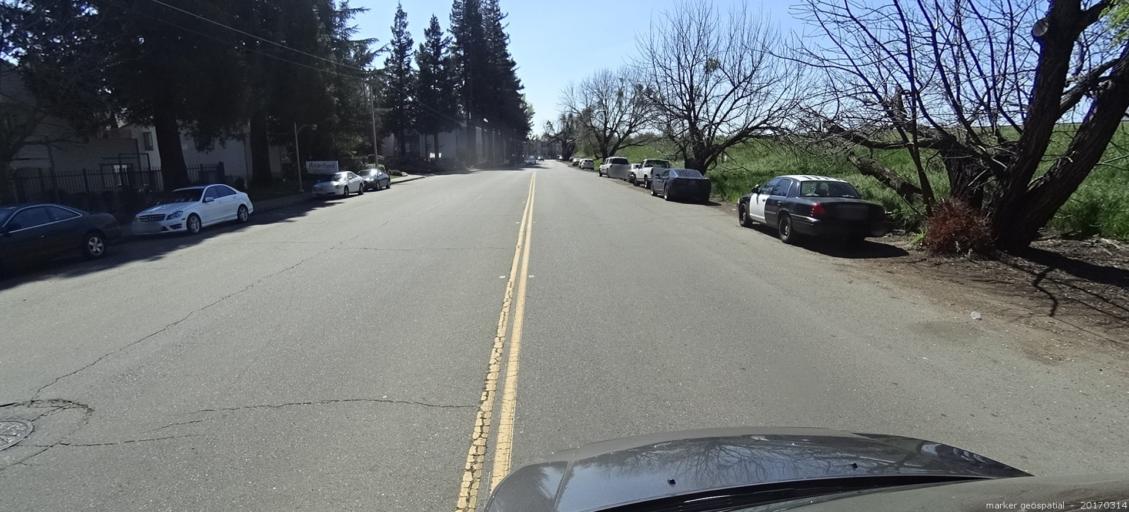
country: US
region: California
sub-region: Yolo County
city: West Sacramento
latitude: 38.5204
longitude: -121.5227
